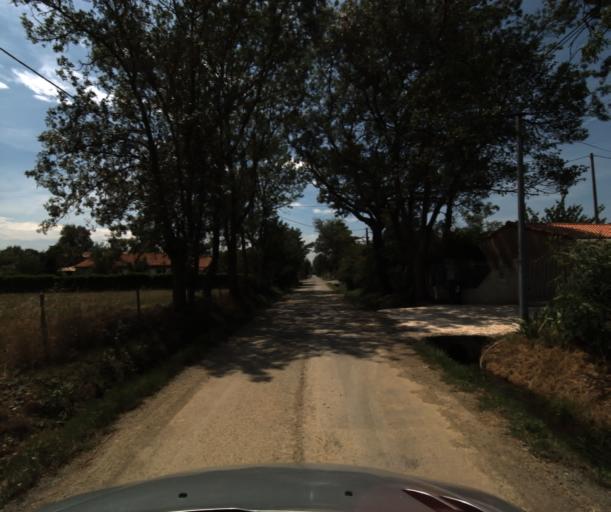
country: FR
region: Midi-Pyrenees
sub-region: Departement de la Haute-Garonne
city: Labastidette
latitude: 43.4523
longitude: 1.2427
